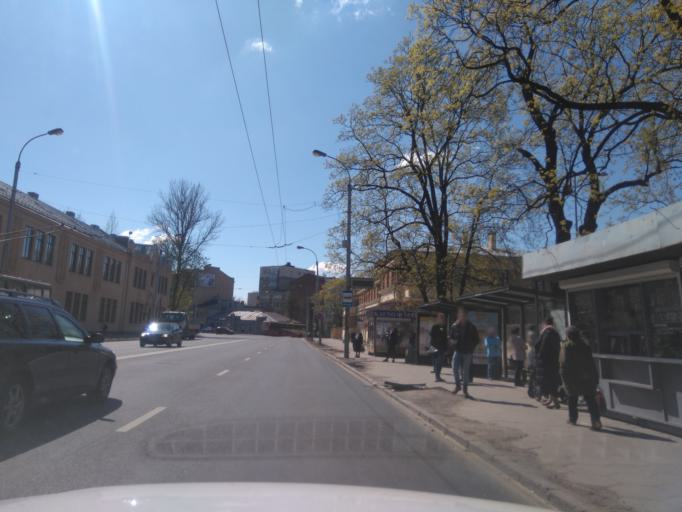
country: LT
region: Kauno apskritis
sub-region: Kaunas
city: Kaunas
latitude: 54.8918
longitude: 23.9247
